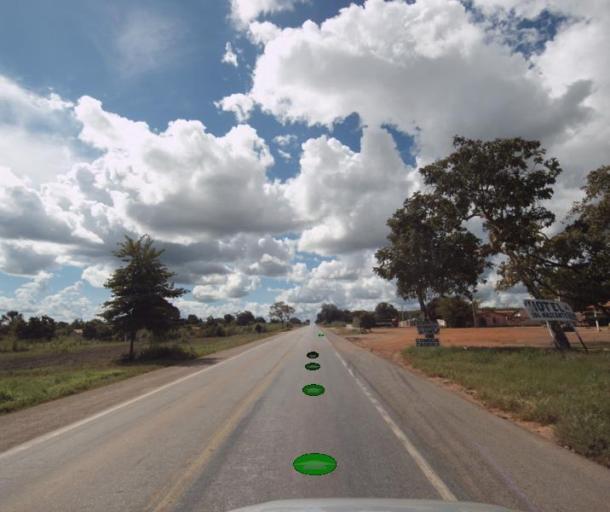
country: BR
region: Goias
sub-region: Porangatu
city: Porangatu
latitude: -13.4267
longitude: -49.1302
